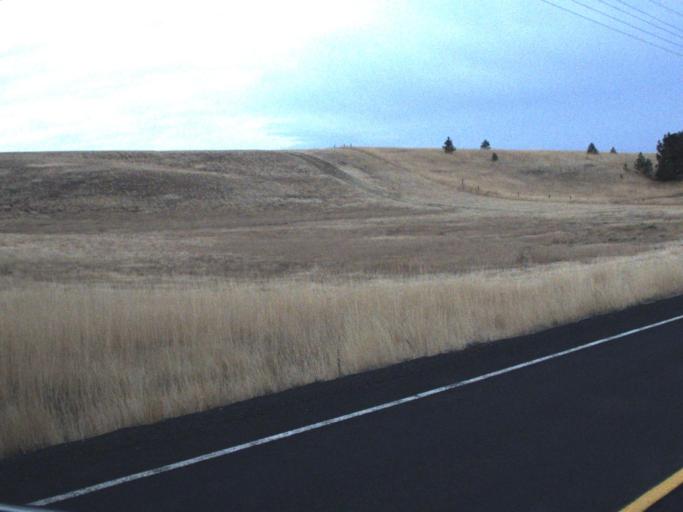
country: US
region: Washington
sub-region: Lincoln County
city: Davenport
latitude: 47.8325
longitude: -118.2104
